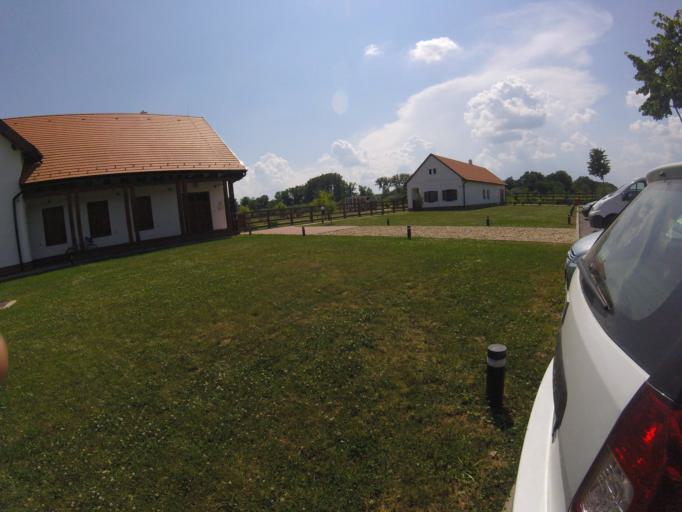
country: HR
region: Osjecko-Baranjska
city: Viljevo
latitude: 45.8004
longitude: 18.0986
